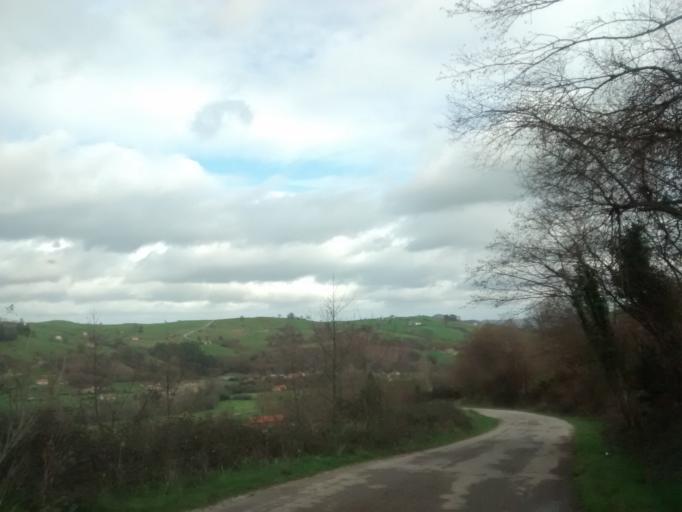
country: ES
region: Cantabria
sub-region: Provincia de Cantabria
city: Lierganes
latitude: 43.3391
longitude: -3.7349
